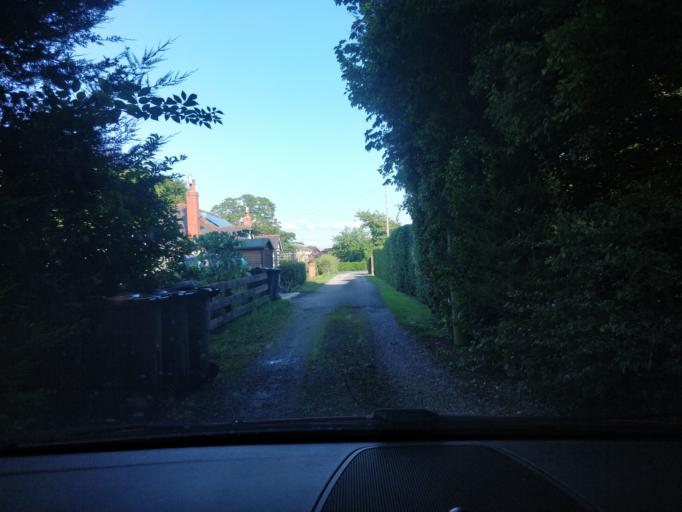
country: GB
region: England
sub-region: Lancashire
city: Banks
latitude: 53.6625
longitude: -2.8815
